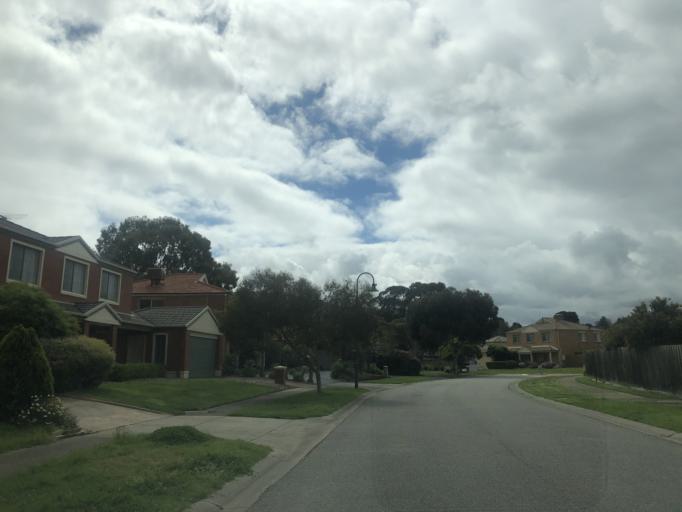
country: AU
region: Victoria
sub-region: Knox
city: Rowville
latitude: -37.9400
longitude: 145.2263
